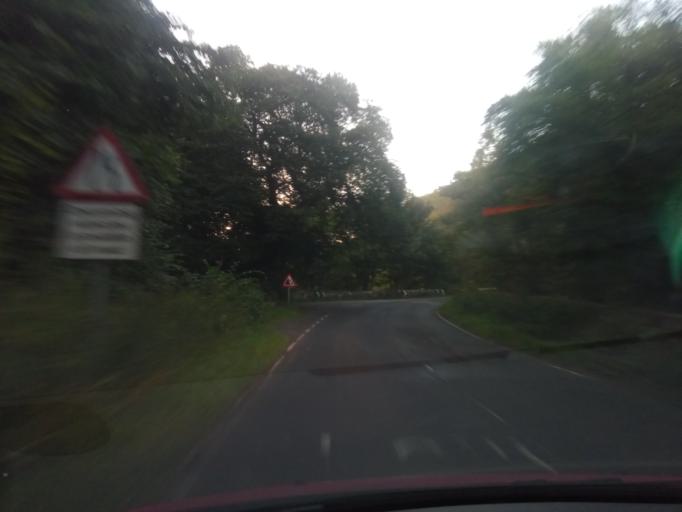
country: GB
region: England
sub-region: Northumberland
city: Bardon Mill
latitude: 54.9259
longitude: -2.3146
